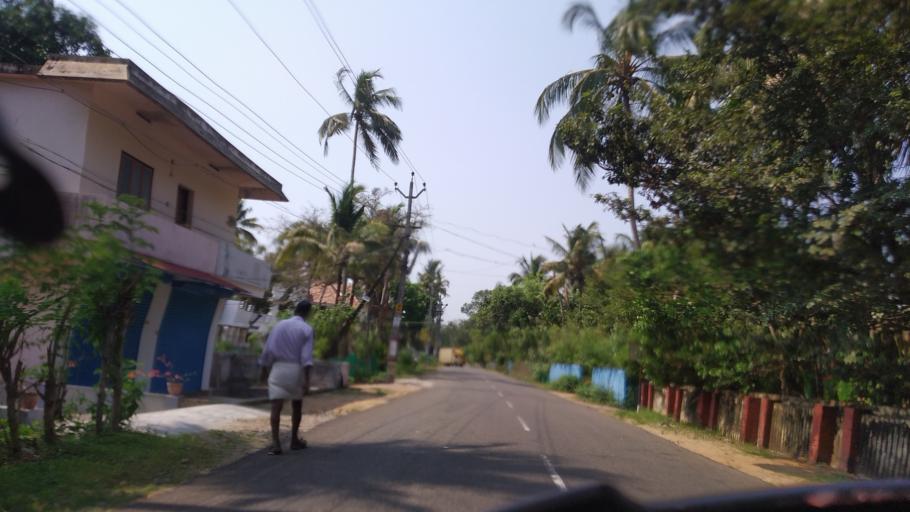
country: IN
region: Kerala
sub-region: Thrissur District
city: Irinjalakuda
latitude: 10.3090
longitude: 76.1283
